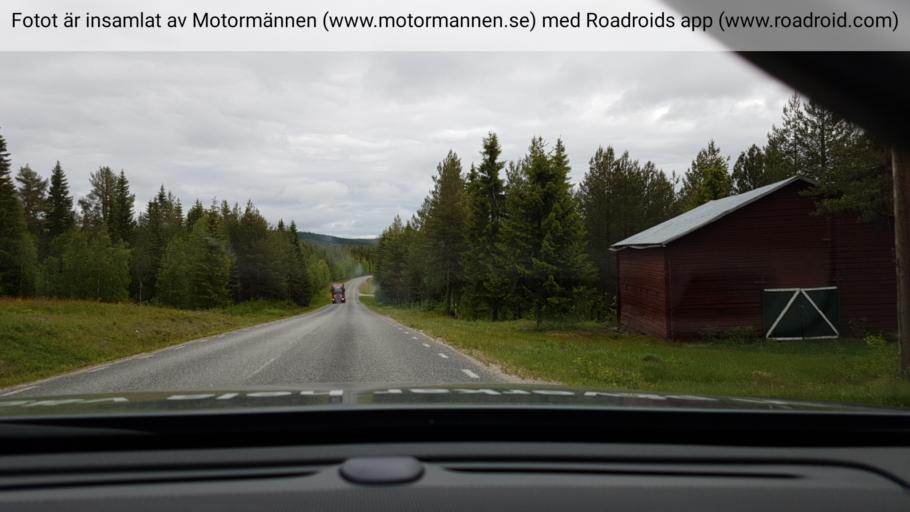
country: SE
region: Vaesterbotten
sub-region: Asele Kommun
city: Insjon
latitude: 64.3316
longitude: 17.7387
